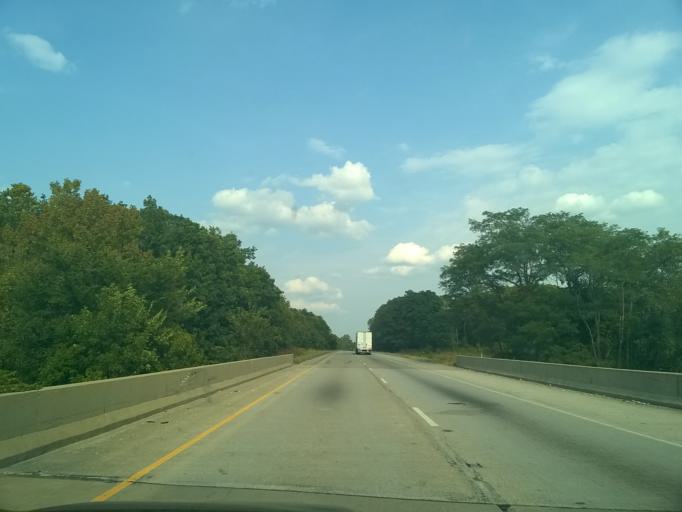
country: US
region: Indiana
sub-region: Vigo County
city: Seelyville
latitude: 39.4448
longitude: -87.2574
